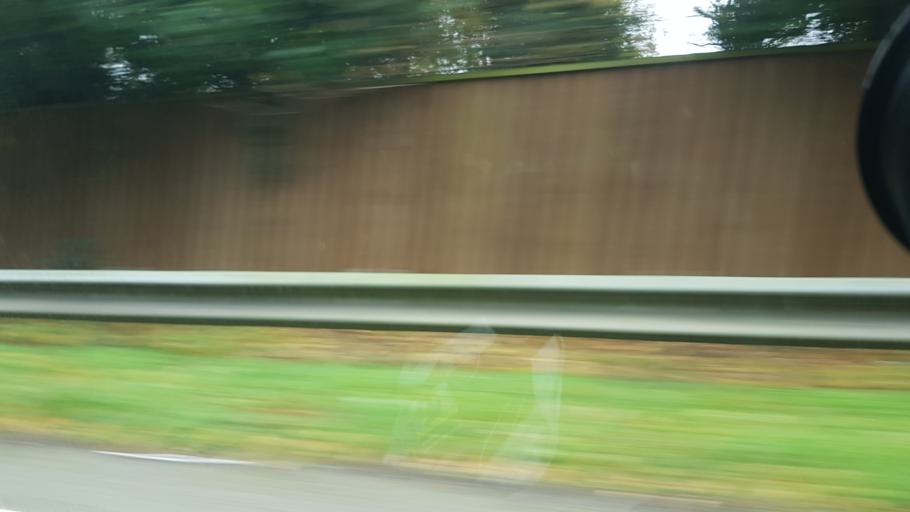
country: GB
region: England
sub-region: Hampshire
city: Fleet
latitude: 51.2974
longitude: -0.7968
